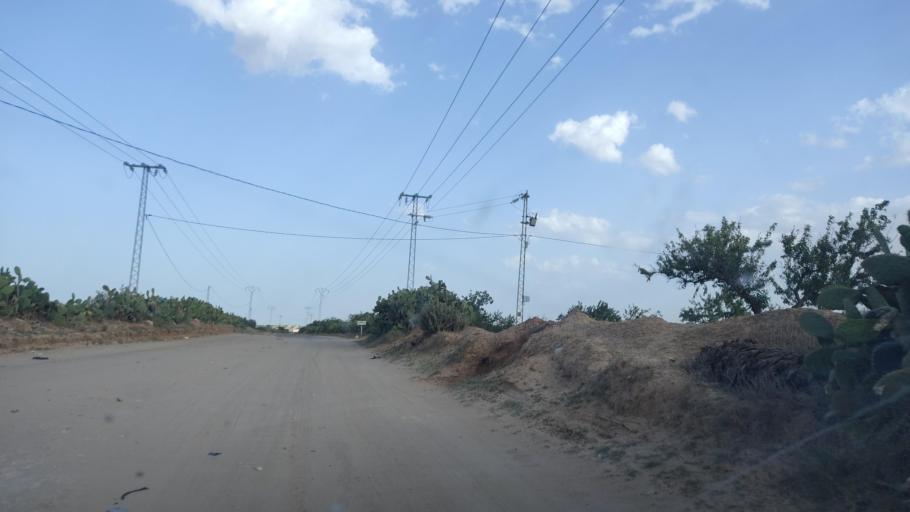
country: TN
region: Safaqis
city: Sfax
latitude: 34.8563
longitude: 10.6052
